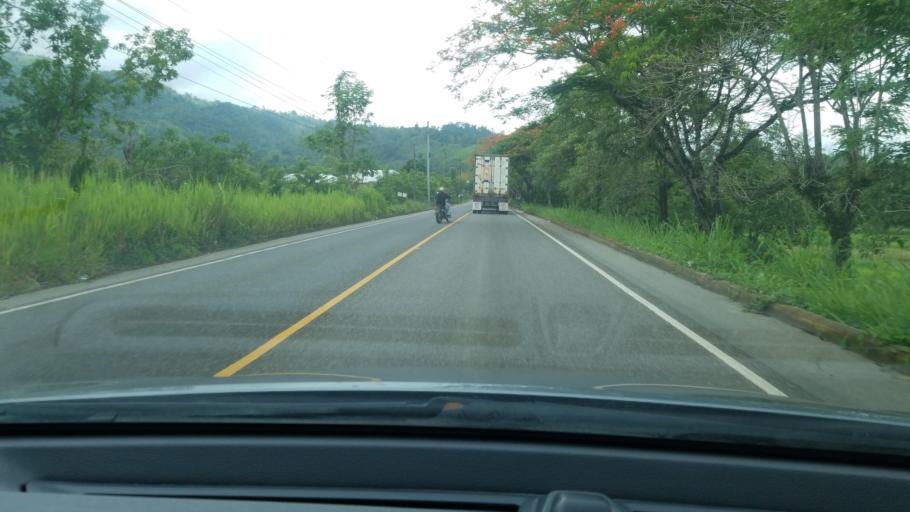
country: HN
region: Cortes
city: Potrerillos
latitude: 15.5895
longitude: -88.3277
